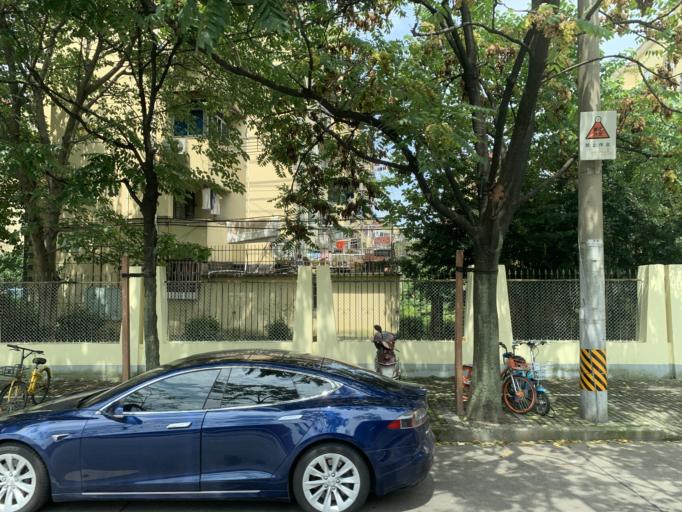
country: CN
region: Shanghai Shi
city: Huamu
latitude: 31.2482
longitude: 121.5763
